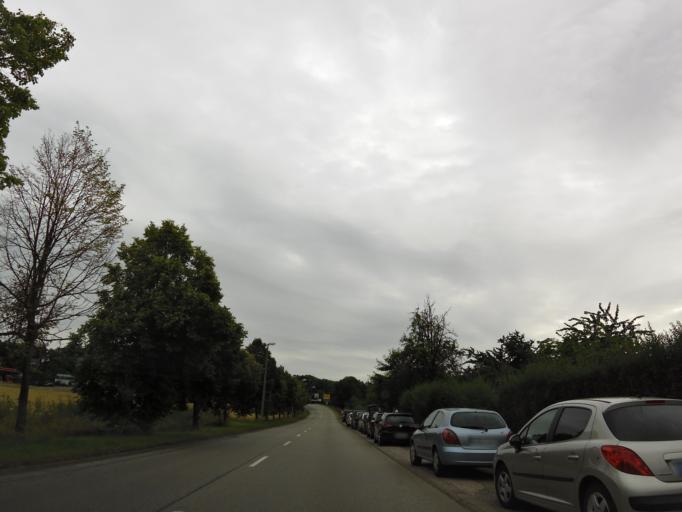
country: DE
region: Thuringia
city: Bad Langensalza
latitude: 51.1156
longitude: 10.6581
